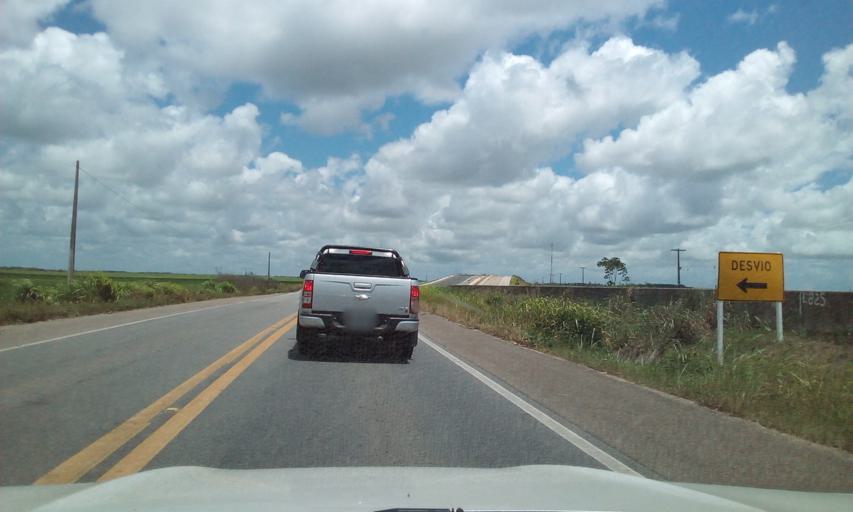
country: BR
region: Alagoas
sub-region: Sao Miguel Dos Campos
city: Sao Miguel dos Campos
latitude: -9.8920
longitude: -36.1928
